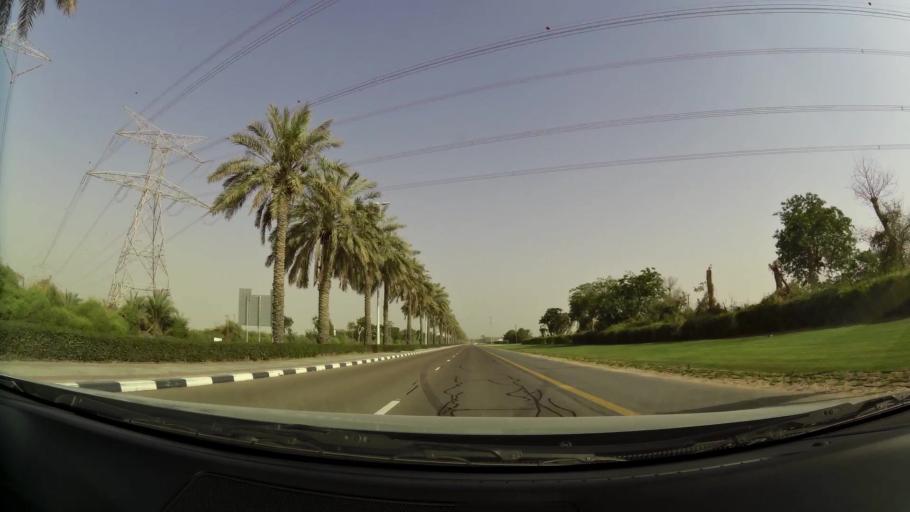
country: AE
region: Dubai
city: Dubai
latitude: 25.1685
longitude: 55.3190
